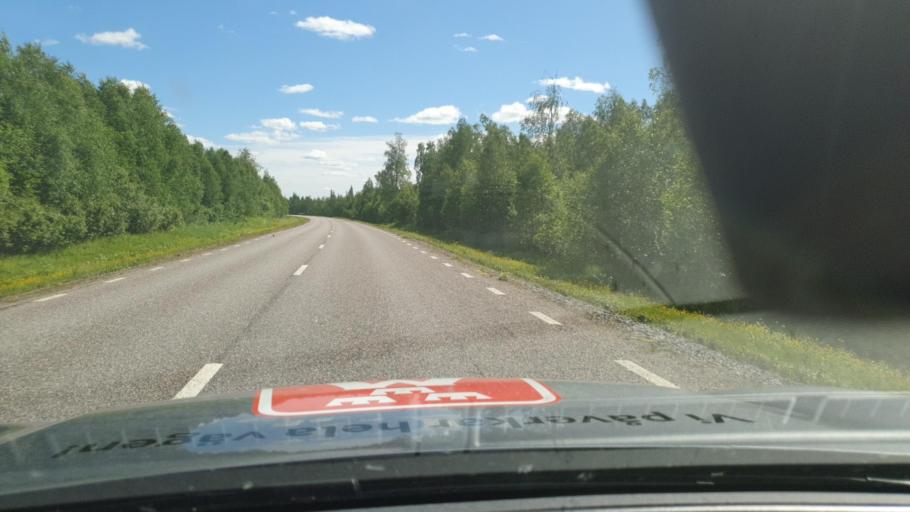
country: SE
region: Norrbotten
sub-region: Pajala Kommun
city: Pajala
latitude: 67.1175
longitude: 23.6100
